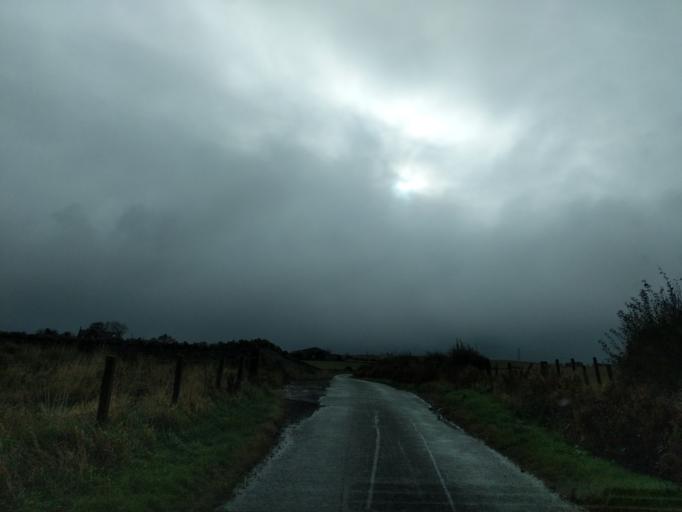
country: GB
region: Scotland
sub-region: East Lothian
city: Dunbar
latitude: 55.9523
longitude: -2.3979
